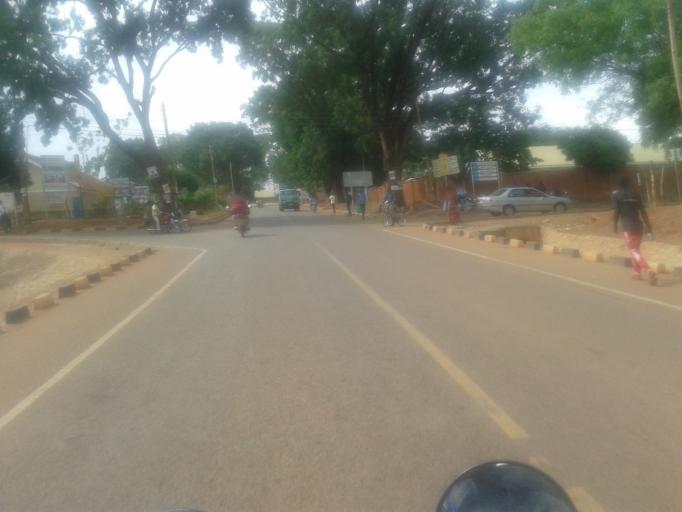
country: UG
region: Northern Region
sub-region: Gulu District
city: Gulu
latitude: 2.7753
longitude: 32.2975
